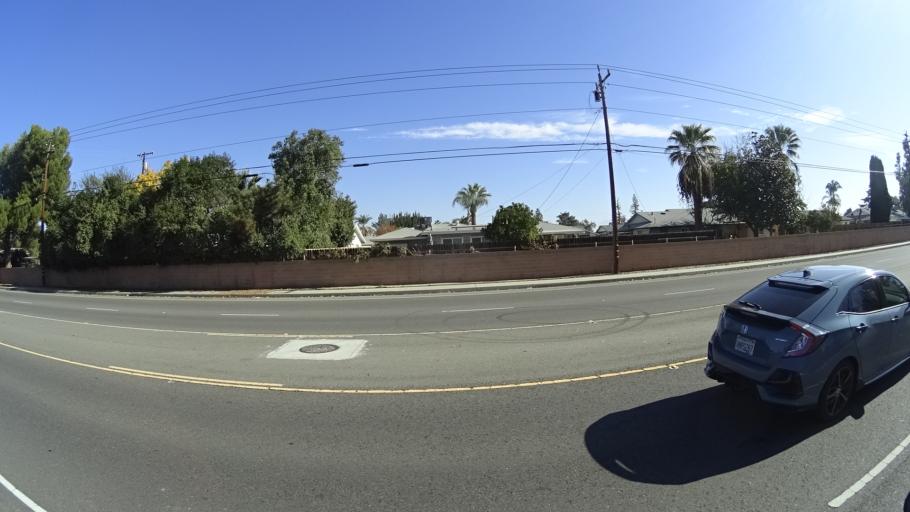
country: US
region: California
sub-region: Kern County
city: Greenacres
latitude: 35.3513
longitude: -119.0737
